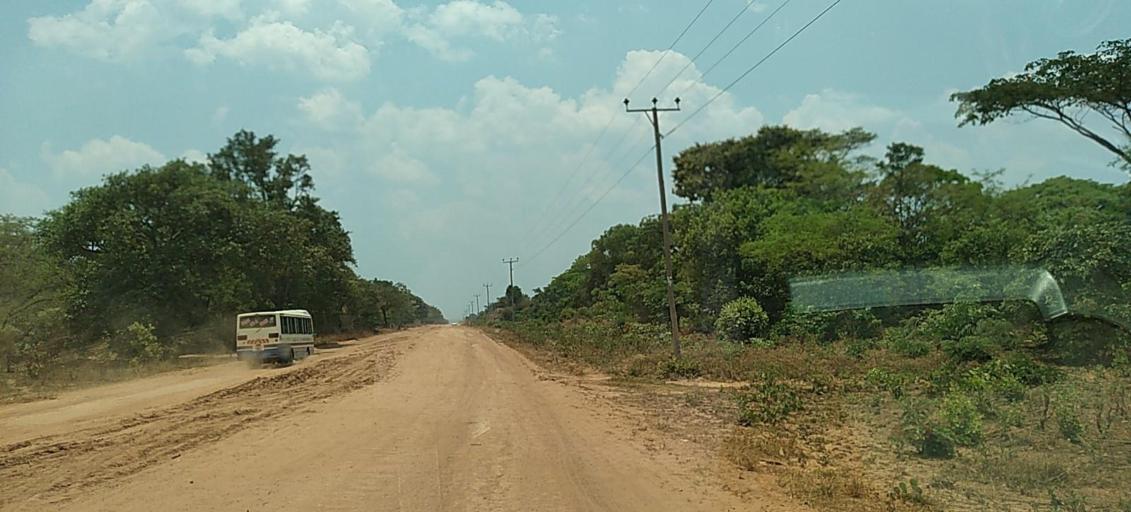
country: ZM
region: Copperbelt
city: Chingola
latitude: -12.9006
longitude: 27.5727
